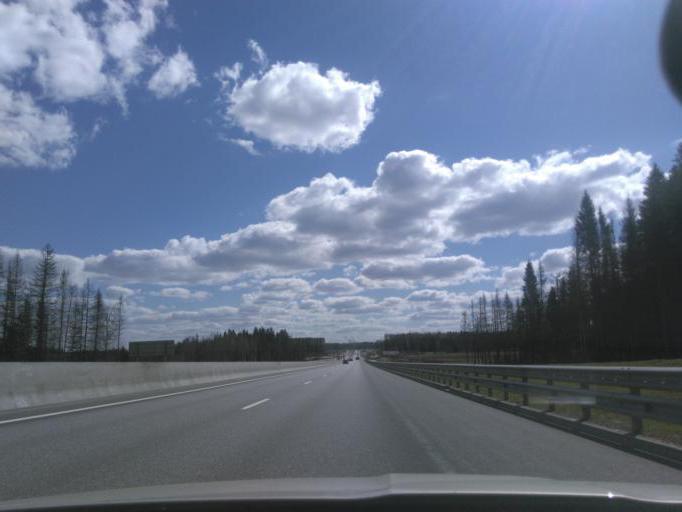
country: RU
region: Moskovskaya
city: Radumlya
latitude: 56.1021
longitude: 37.1511
